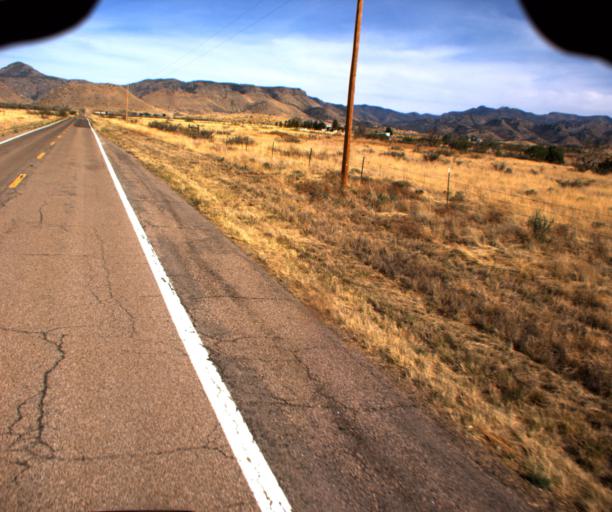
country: US
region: Arizona
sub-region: Cochise County
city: Willcox
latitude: 32.0067
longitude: -109.4204
